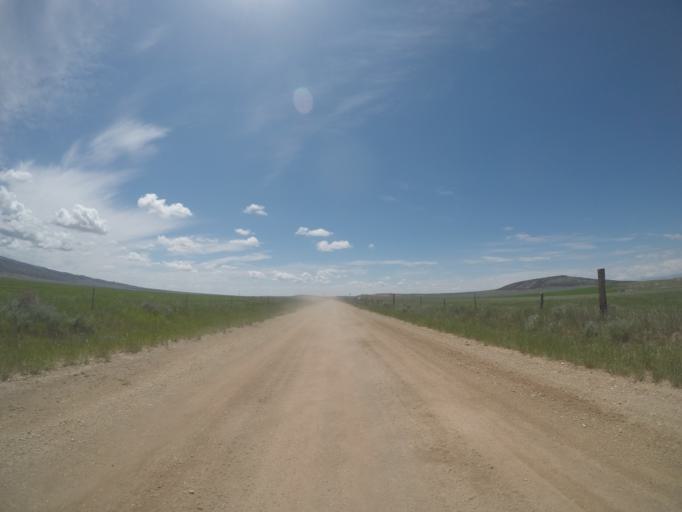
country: US
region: Wyoming
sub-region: Park County
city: Powell
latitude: 45.2085
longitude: -108.7190
